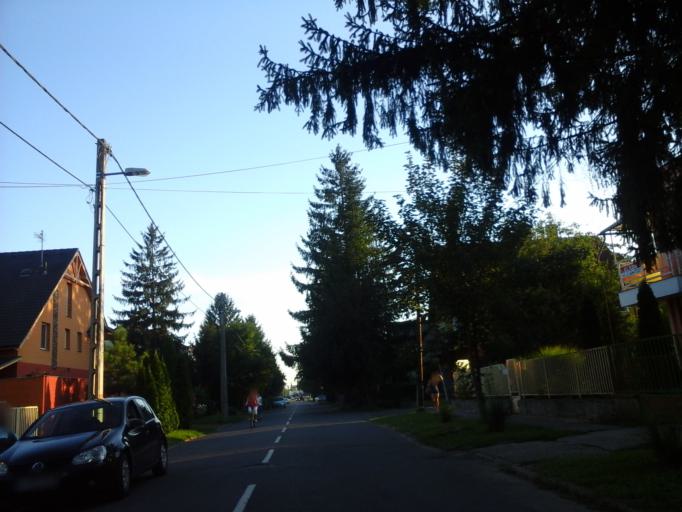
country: HU
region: Hajdu-Bihar
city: Hajduszoboszlo
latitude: 47.4572
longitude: 21.4041
